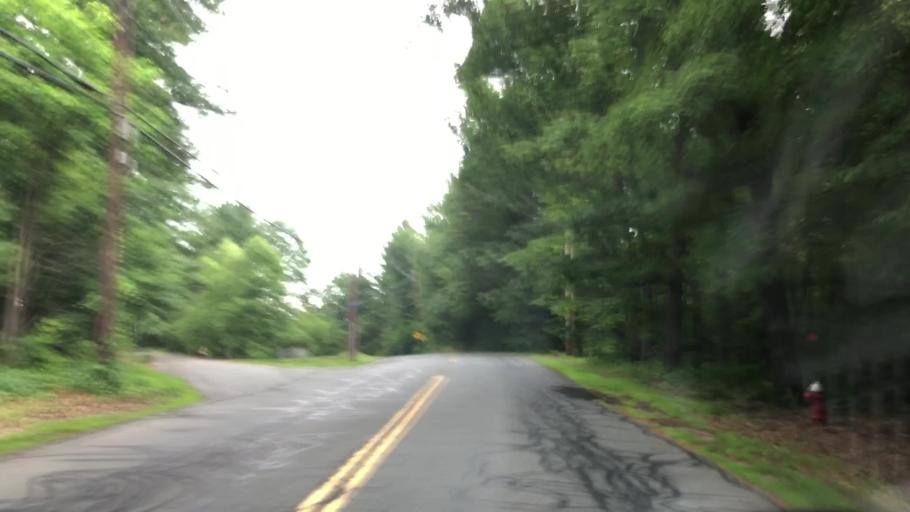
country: US
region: Massachusetts
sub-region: Hampden County
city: Holyoke
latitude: 42.1876
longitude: -72.6675
